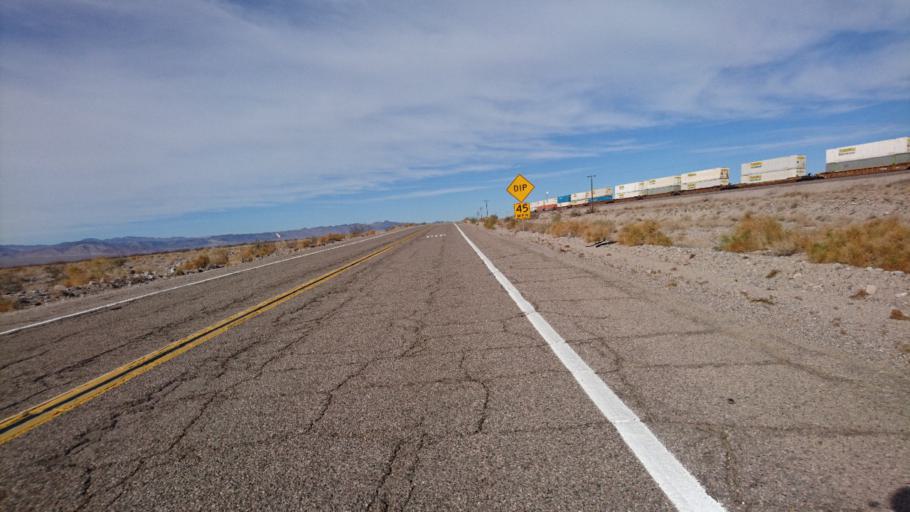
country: US
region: California
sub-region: San Bernardino County
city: Twentynine Palms
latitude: 34.6019
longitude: -115.9527
